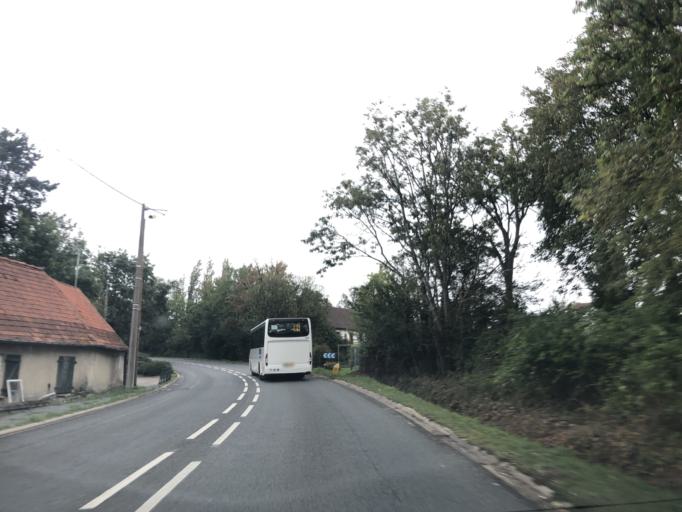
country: FR
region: Nord-Pas-de-Calais
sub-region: Departement du Pas-de-Calais
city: Rang-du-Fliers
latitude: 50.4356
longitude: 1.6518
